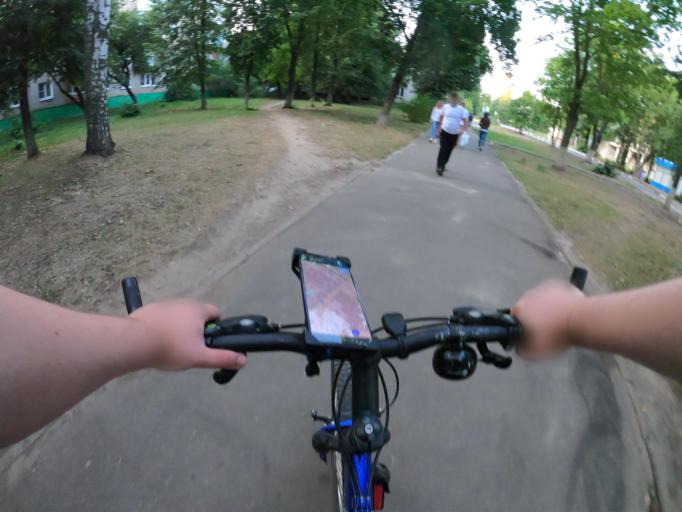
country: RU
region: Moskovskaya
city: Beloozerskiy
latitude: 55.4580
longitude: 38.4455
